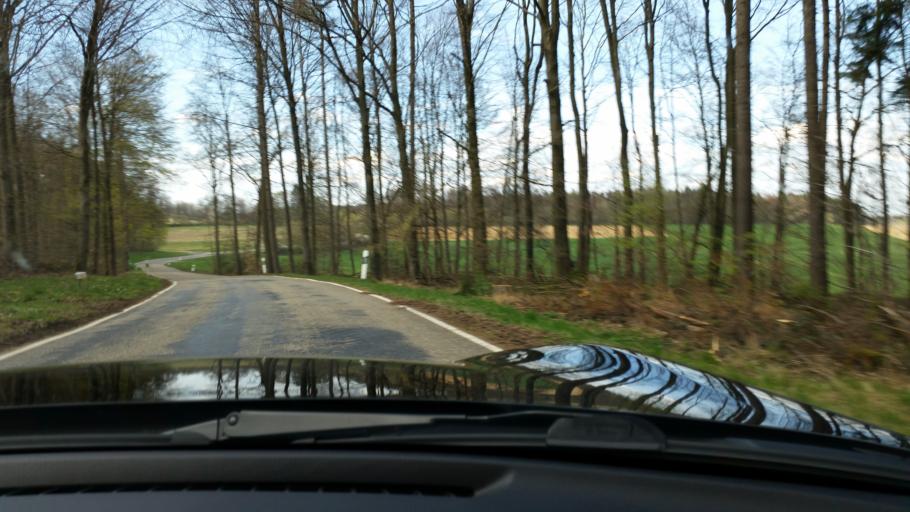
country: DE
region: Baden-Wuerttemberg
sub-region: Regierungsbezirk Stuttgart
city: Widdern
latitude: 49.3457
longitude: 9.4124
